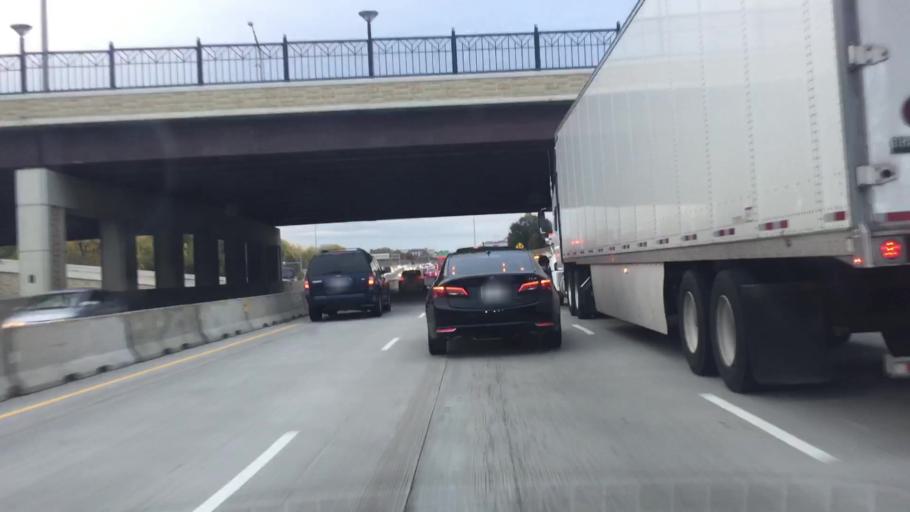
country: US
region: Kansas
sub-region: Johnson County
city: Lenexa
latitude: 38.9363
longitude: -94.6916
